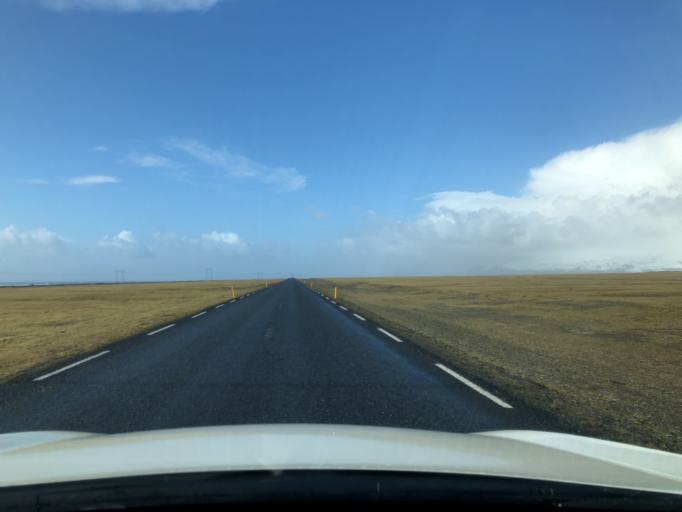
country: IS
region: East
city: Hoefn
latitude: 64.0623
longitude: -16.1415
